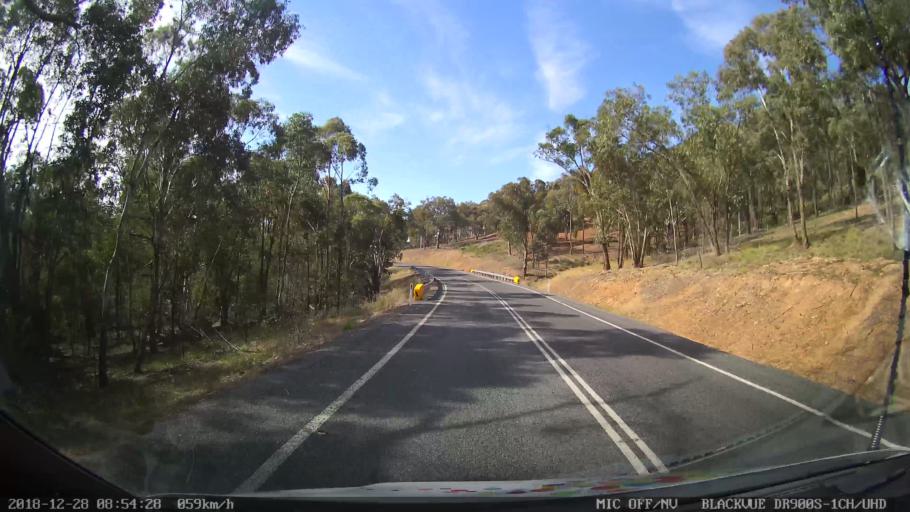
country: AU
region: New South Wales
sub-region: Upper Lachlan Shire
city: Crookwell
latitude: -34.0921
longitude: 149.3322
